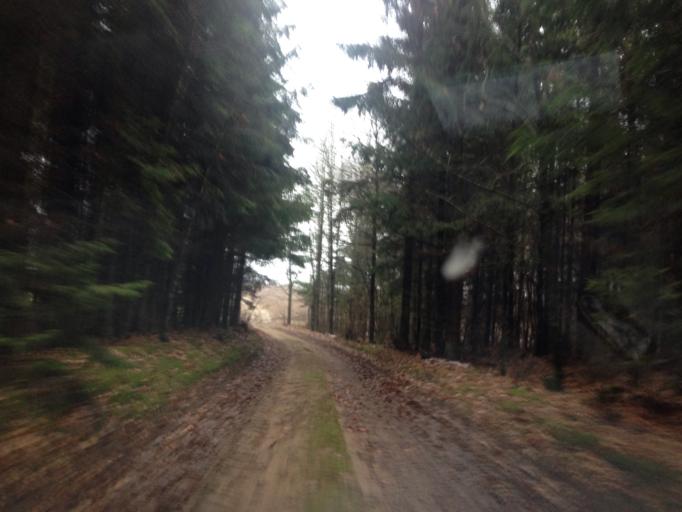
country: PL
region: Warmian-Masurian Voivodeship
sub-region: Powiat ketrzynski
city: Ketrzyn
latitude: 54.0317
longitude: 21.4153
